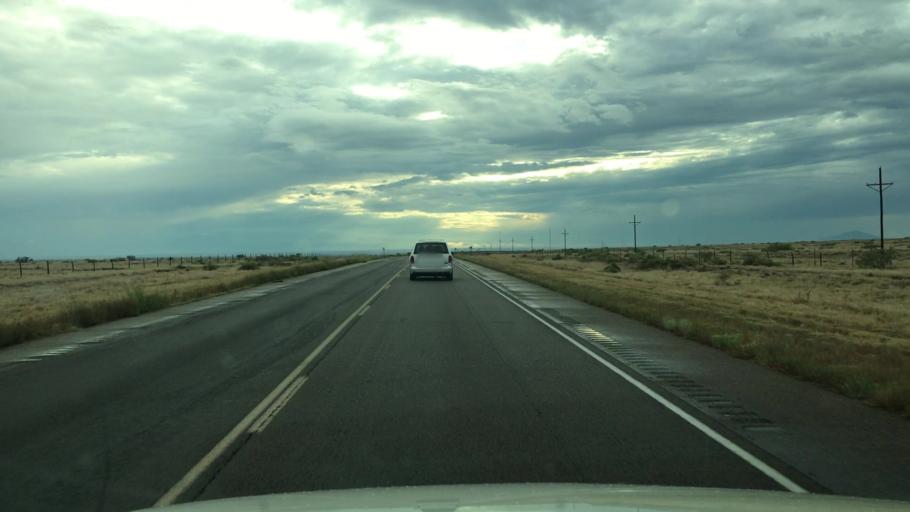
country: US
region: New Mexico
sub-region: Chaves County
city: Roswell
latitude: 33.4014
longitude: -104.3341
